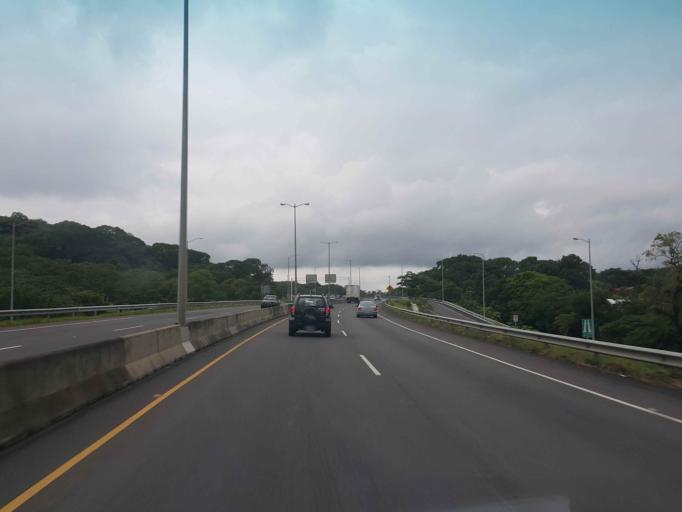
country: CR
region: Alajuela
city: Atenas
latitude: 9.9437
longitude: -84.3772
